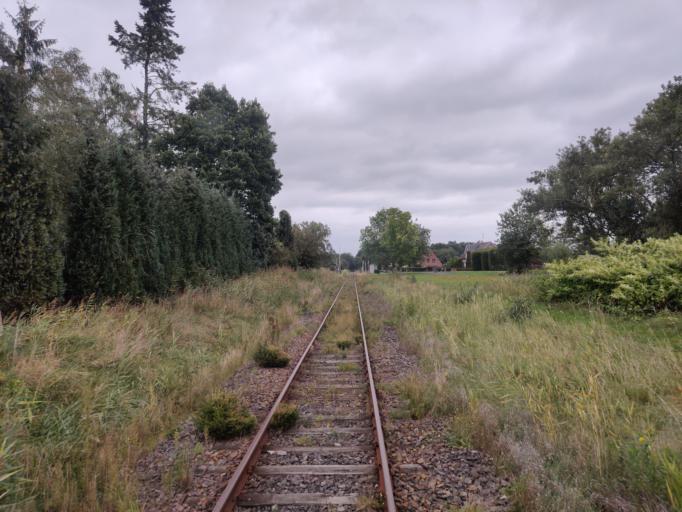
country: DE
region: Lower Saxony
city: Gnarrenburg
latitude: 53.4136
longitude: 9.0132
